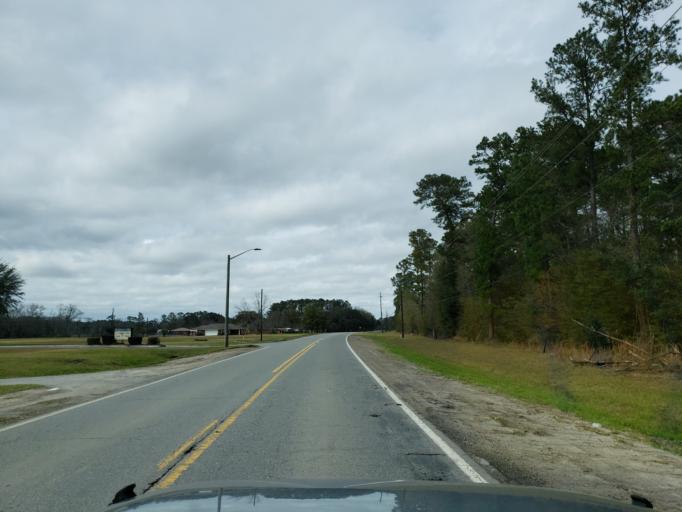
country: US
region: Georgia
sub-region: Chatham County
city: Georgetown
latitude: 32.0183
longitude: -81.2627
